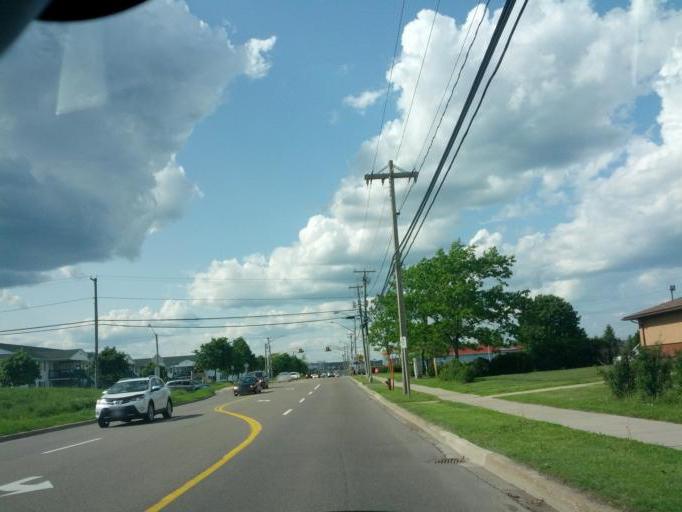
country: CA
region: New Brunswick
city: Moncton
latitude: 46.1099
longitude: -64.8237
